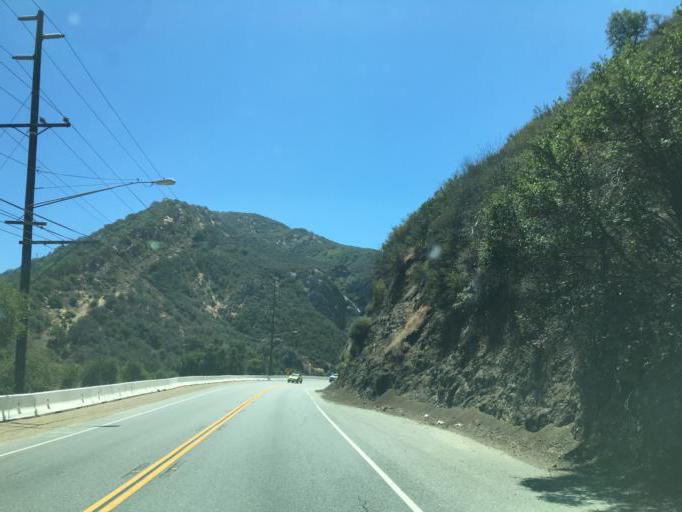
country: US
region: California
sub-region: Los Angeles County
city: Malibu Beach
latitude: 34.0790
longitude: -118.7029
